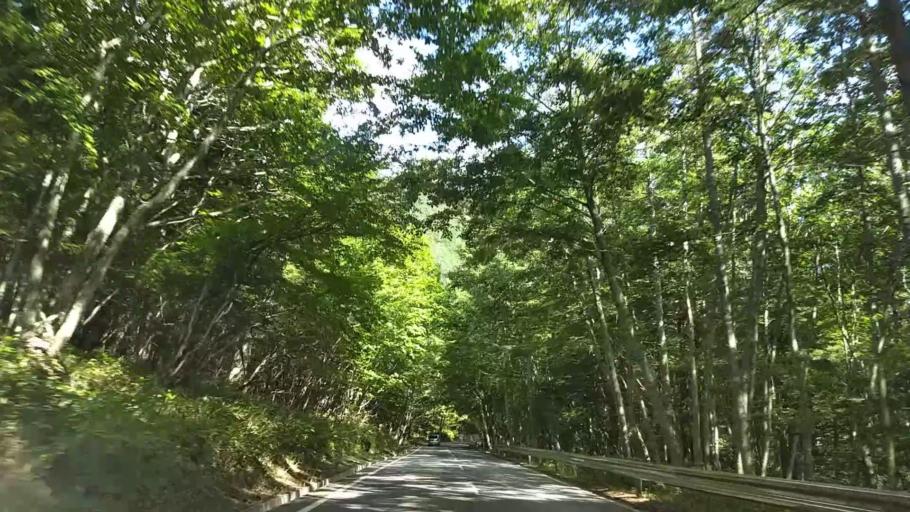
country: JP
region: Nagano
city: Chino
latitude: 36.1092
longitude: 138.2726
